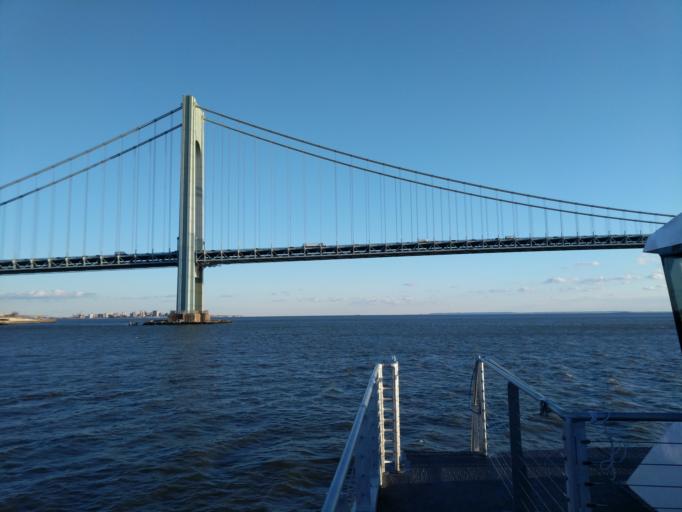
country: US
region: New York
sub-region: Kings County
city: Bensonhurst
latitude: 40.6121
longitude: -74.0419
